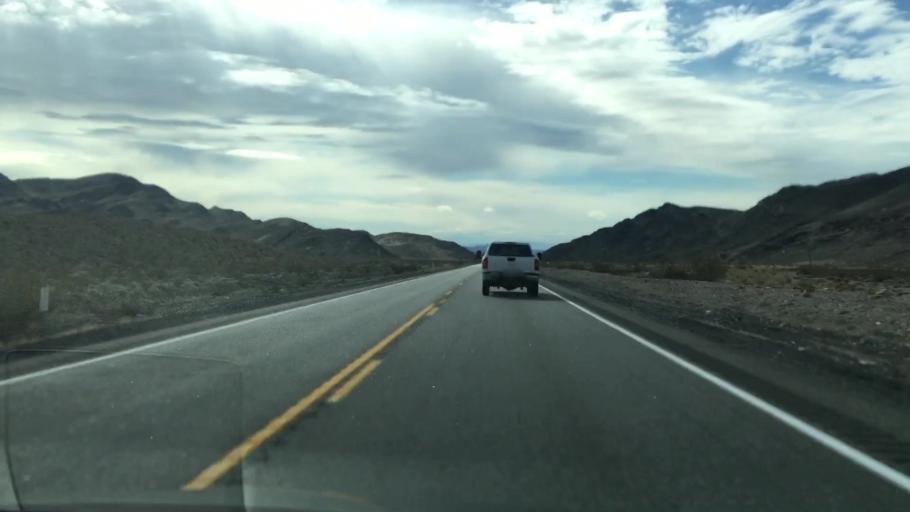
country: US
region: Nevada
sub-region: Nye County
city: Pahrump
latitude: 36.5798
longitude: -116.0673
